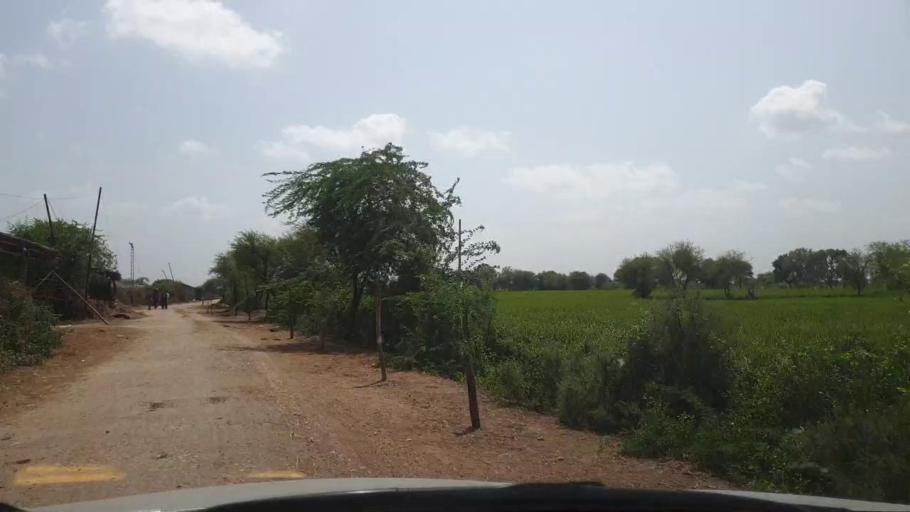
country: PK
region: Sindh
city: Talhar
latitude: 24.8982
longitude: 68.9062
